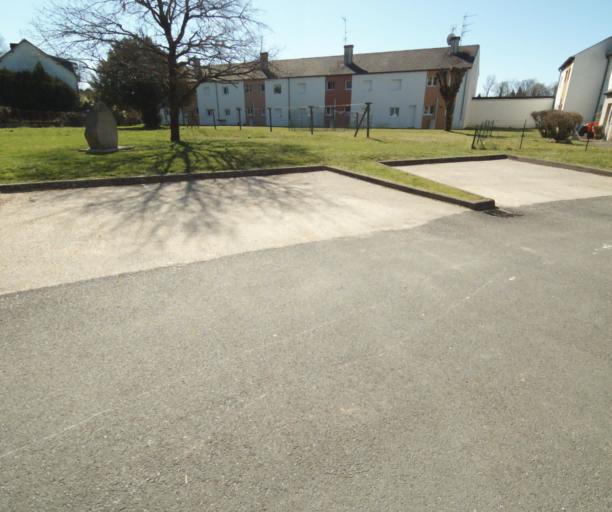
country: FR
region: Limousin
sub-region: Departement de la Correze
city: Chamboulive
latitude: 45.4313
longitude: 1.7042
